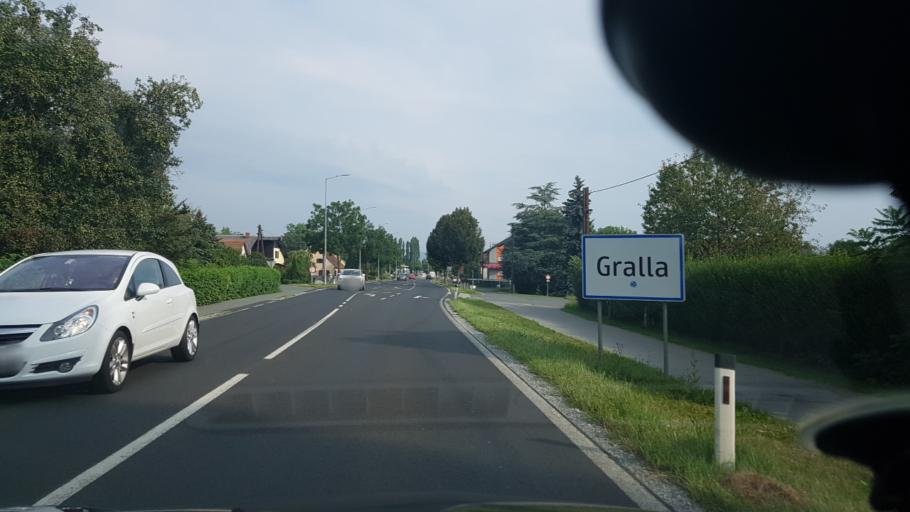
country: AT
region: Styria
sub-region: Politischer Bezirk Leibnitz
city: Kaindorf an der Sulm
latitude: 46.8008
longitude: 15.5560
